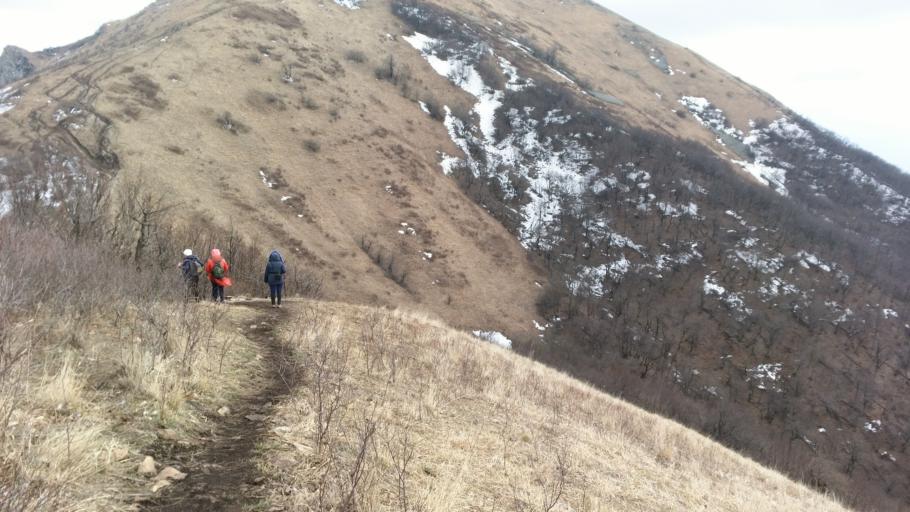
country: RU
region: Stavropol'skiy
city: Zheleznovodsk
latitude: 44.1051
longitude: 43.0192
